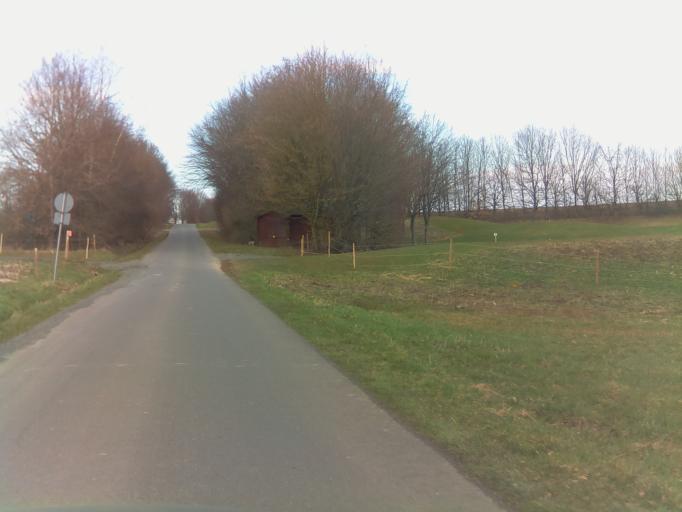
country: DE
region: Rheinland-Pfalz
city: Siesbach
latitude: 49.7486
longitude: 7.2289
